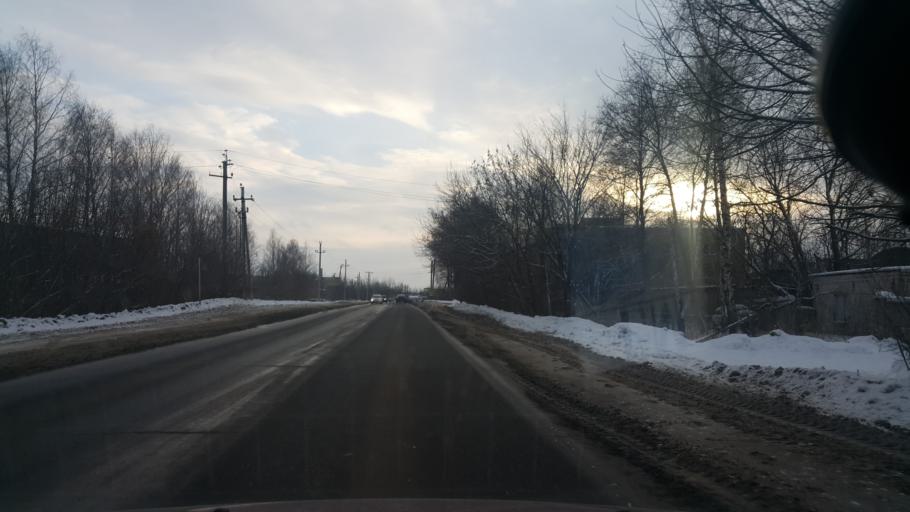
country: RU
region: Tambov
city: Pokrovo-Prigorodnoye
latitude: 52.6574
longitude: 41.4231
